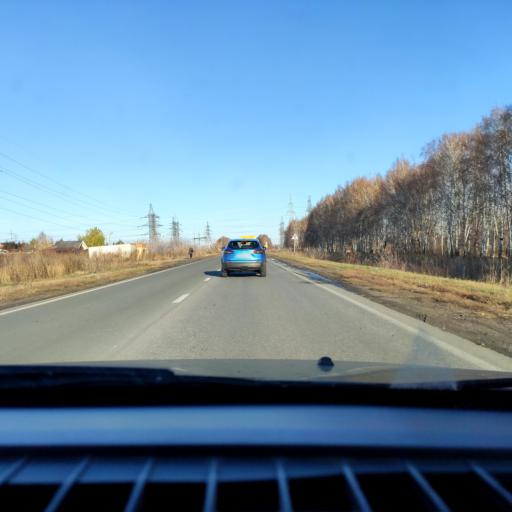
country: RU
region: Samara
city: Tol'yatti
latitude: 53.5839
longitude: 49.3337
